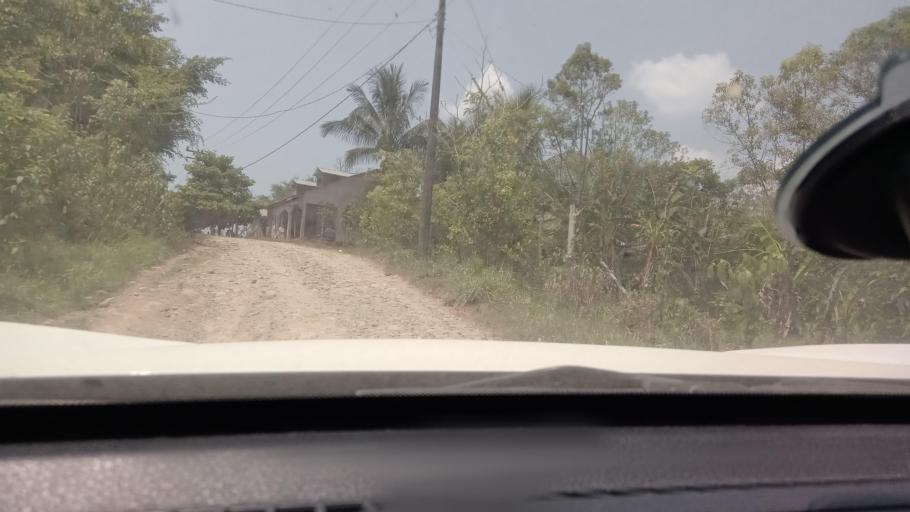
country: MX
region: Tabasco
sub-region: Huimanguillo
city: Francisco Rueda
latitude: 17.4826
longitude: -93.9436
